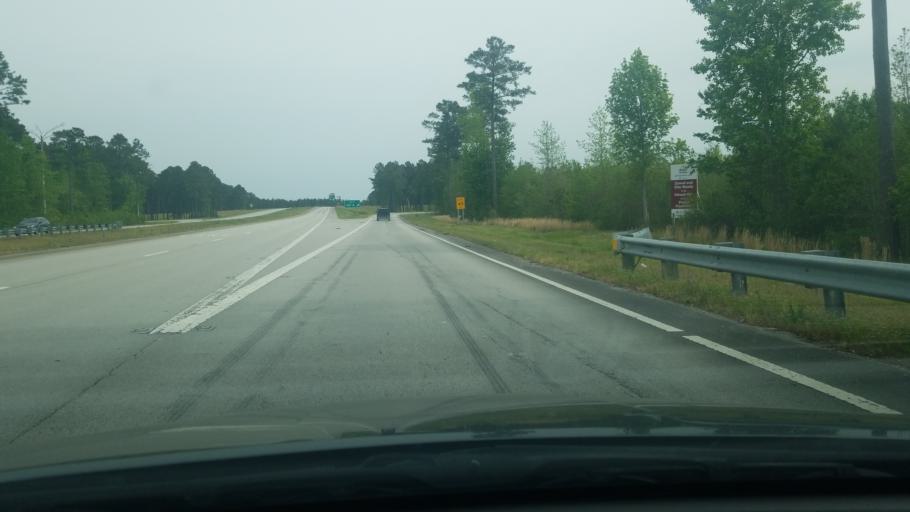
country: US
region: North Carolina
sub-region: Craven County
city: River Bend
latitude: 35.1265
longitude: -77.1535
